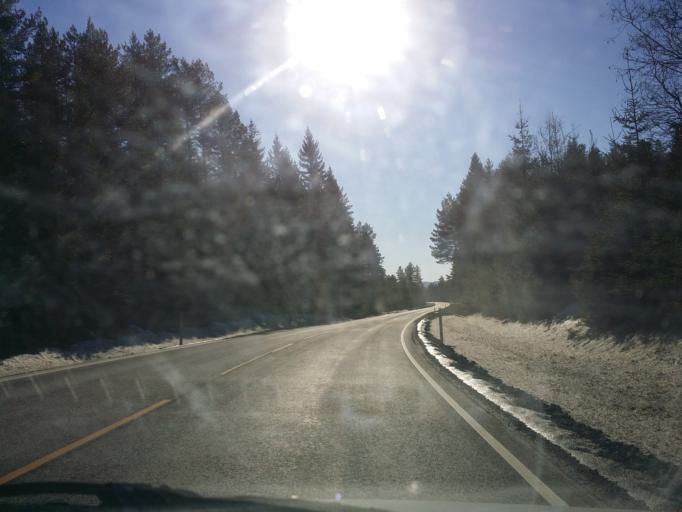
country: NO
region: Buskerud
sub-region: Ringerike
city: Honefoss
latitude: 60.2814
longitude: 10.1953
